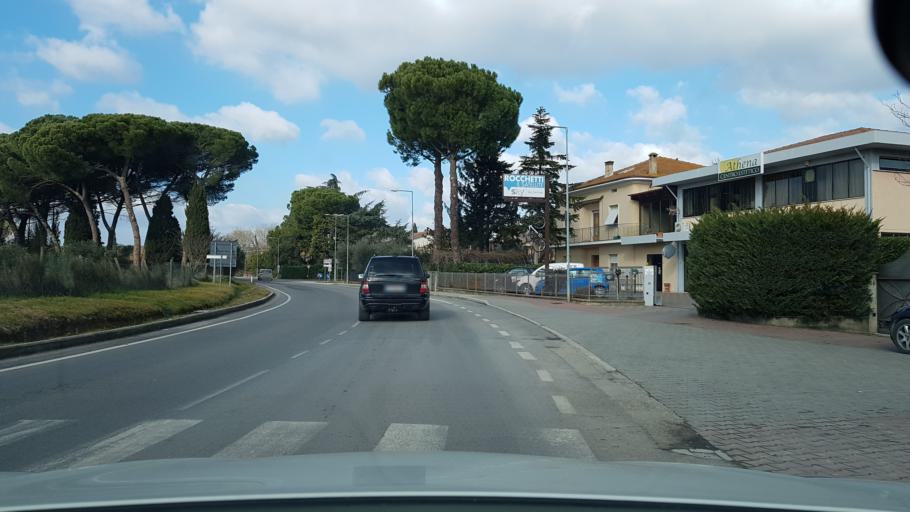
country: IT
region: Umbria
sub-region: Provincia di Perugia
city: Castiglione del Lago
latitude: 43.1302
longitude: 12.0428
